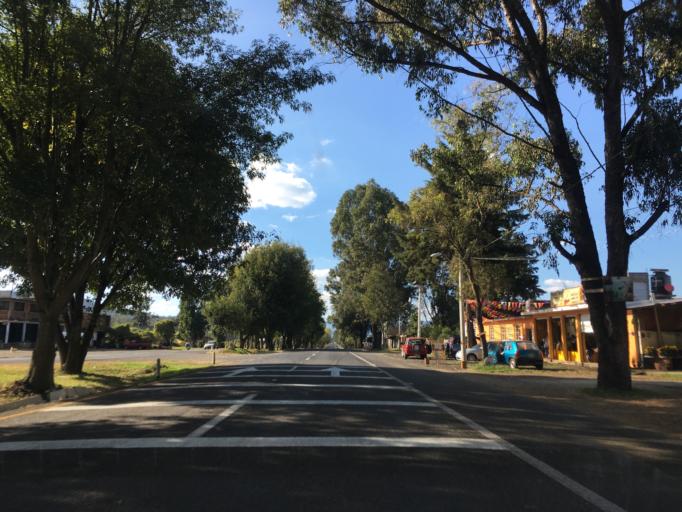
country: MX
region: Michoacan
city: Patzcuaro
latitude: 19.5373
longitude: -101.5738
